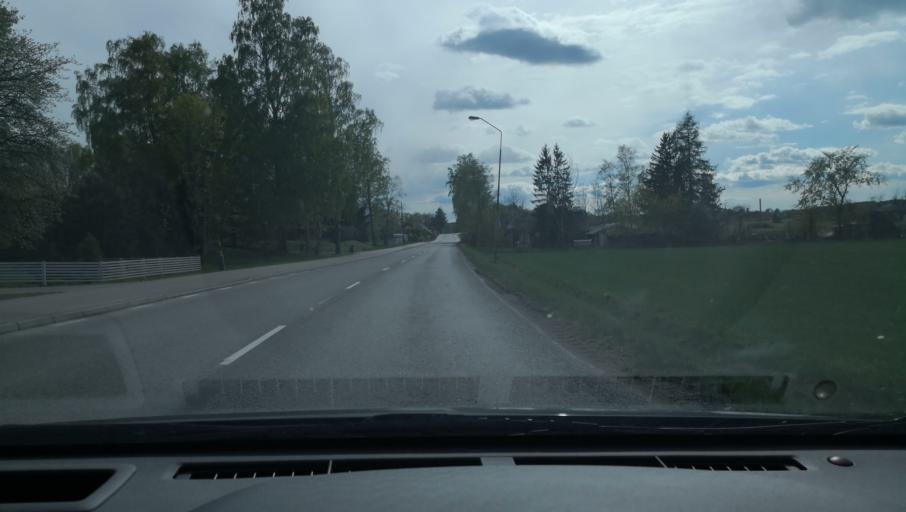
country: SE
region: OErebro
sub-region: Hallsbergs Kommun
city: Hallsberg
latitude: 59.0752
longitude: 15.1421
